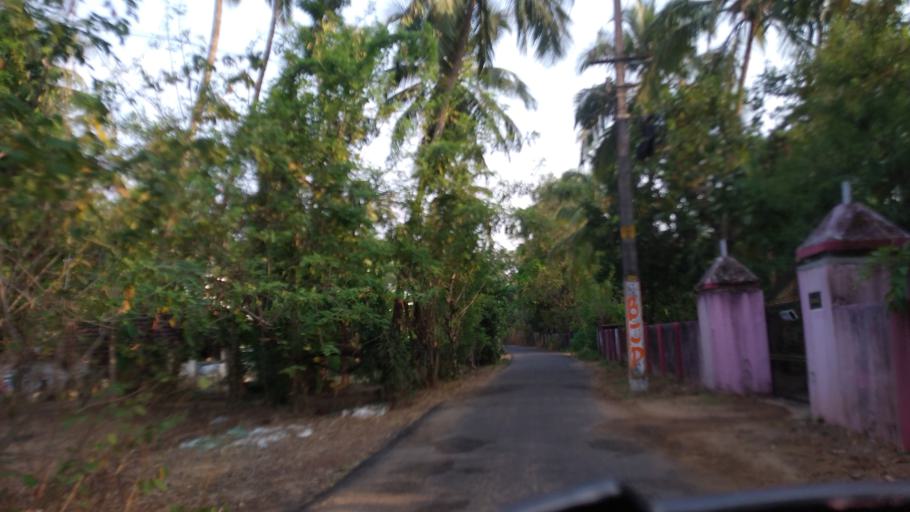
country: IN
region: Kerala
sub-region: Thrissur District
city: Thanniyam
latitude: 10.4283
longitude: 76.0806
